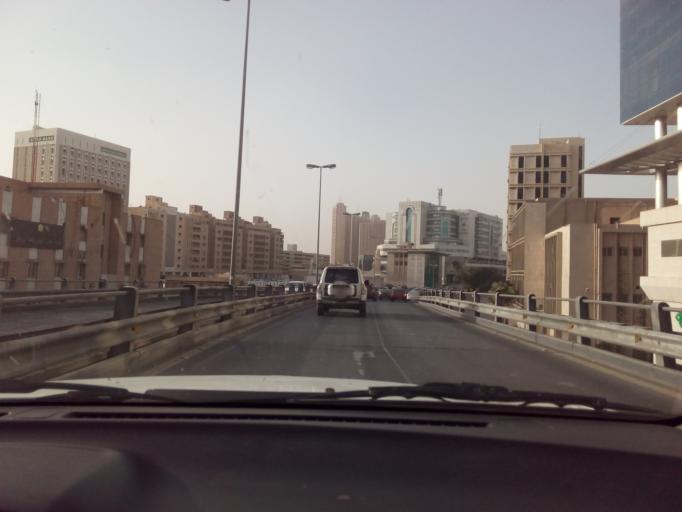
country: SA
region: Ar Riyad
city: Riyadh
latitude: 24.6302
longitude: 46.7172
